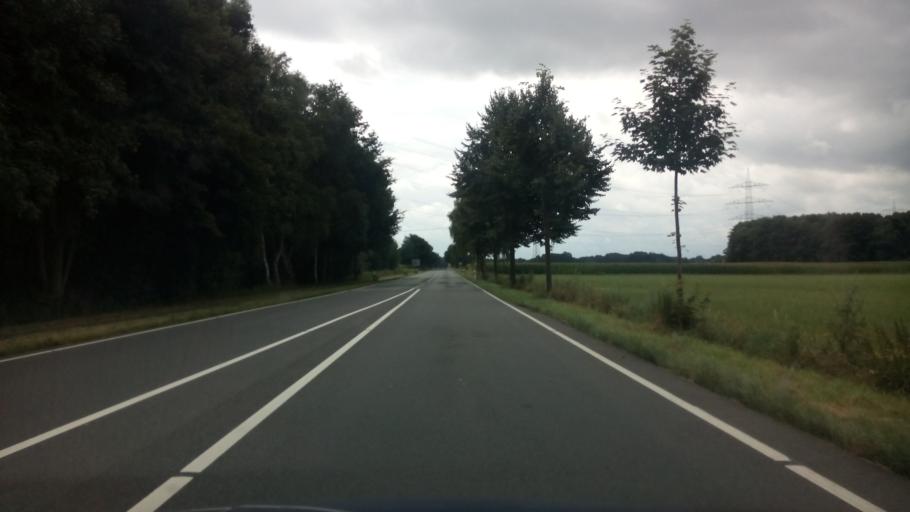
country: DE
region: Lower Saxony
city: Marl
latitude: 52.4807
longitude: 8.3681
